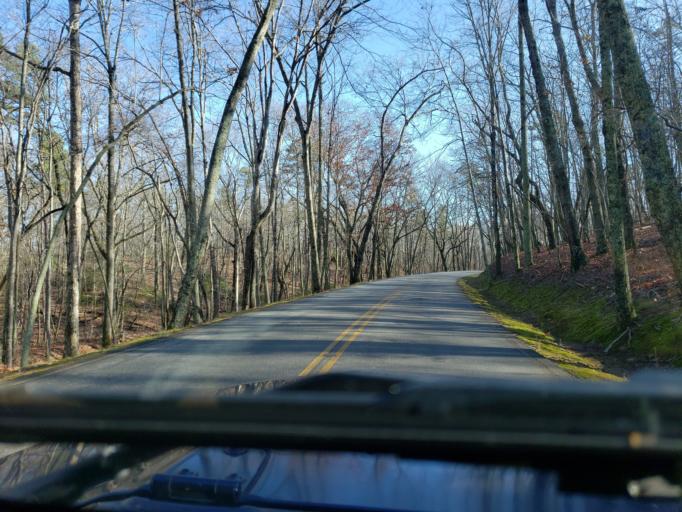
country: US
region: North Carolina
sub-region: Cleveland County
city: White Plains
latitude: 35.1482
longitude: -81.3885
